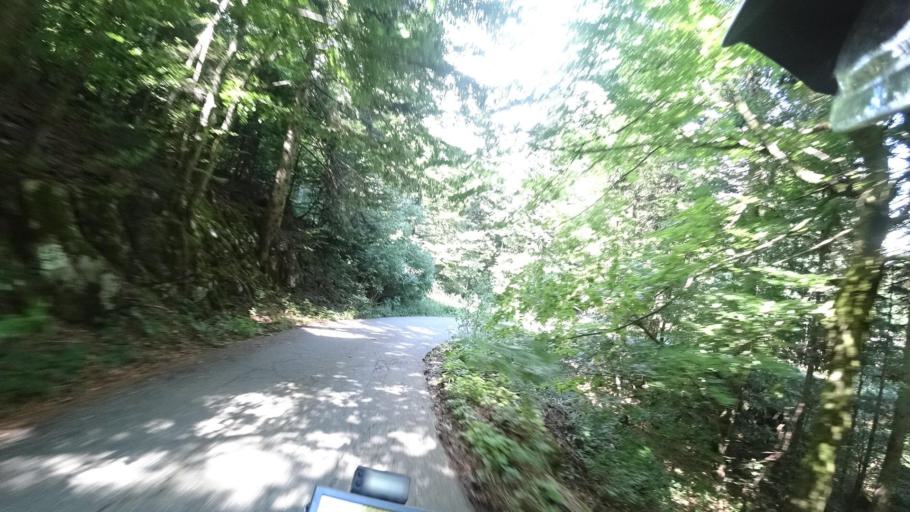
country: HR
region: Licko-Senjska
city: Brinje
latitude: 45.1092
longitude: 15.0343
